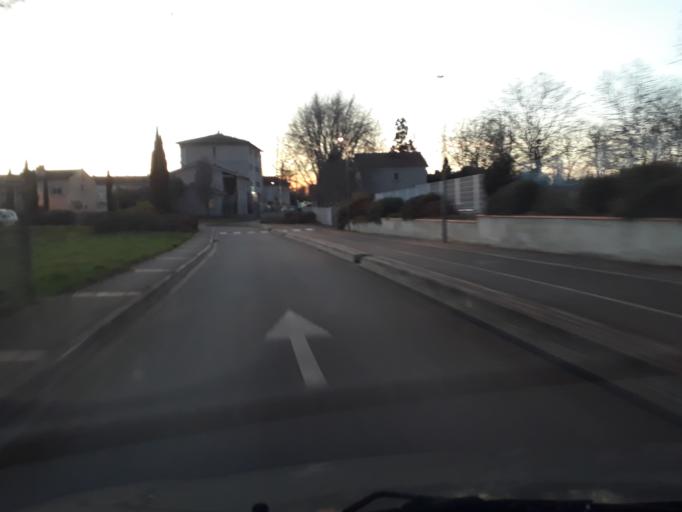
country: FR
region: Midi-Pyrenees
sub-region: Departement de la Haute-Garonne
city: Carbonne
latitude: 43.3005
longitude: 1.2268
